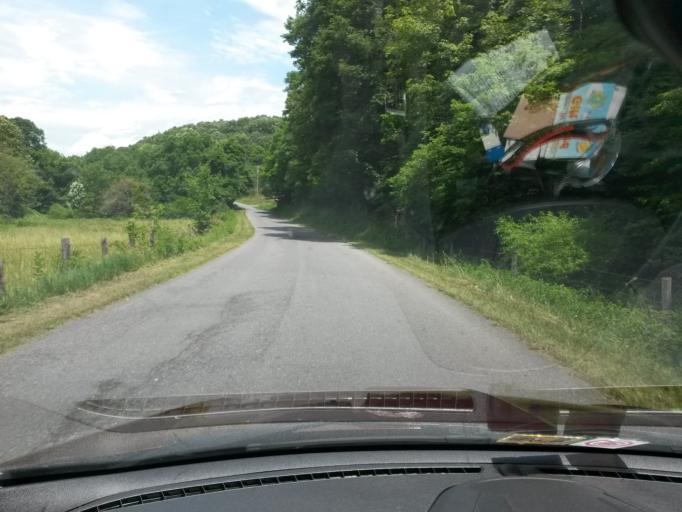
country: US
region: West Virginia
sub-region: Monroe County
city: Union
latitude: 37.5277
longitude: -80.5469
